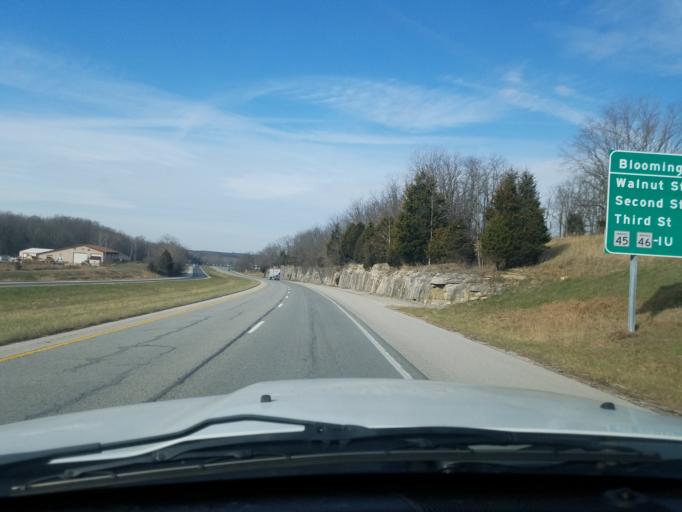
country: US
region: Indiana
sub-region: Monroe County
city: Bloomington
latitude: 39.0801
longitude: -86.5374
